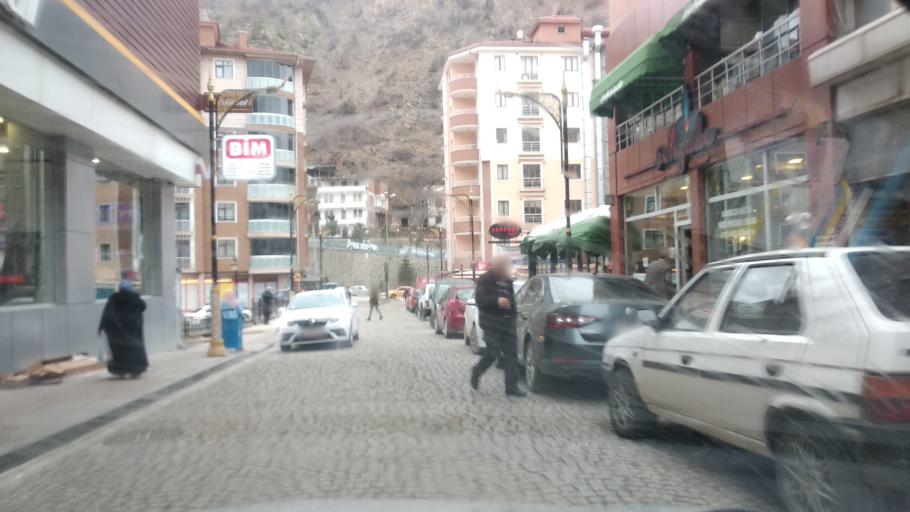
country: TR
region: Gumushane
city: Gumushkhane
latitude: 40.4584
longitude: 39.4806
